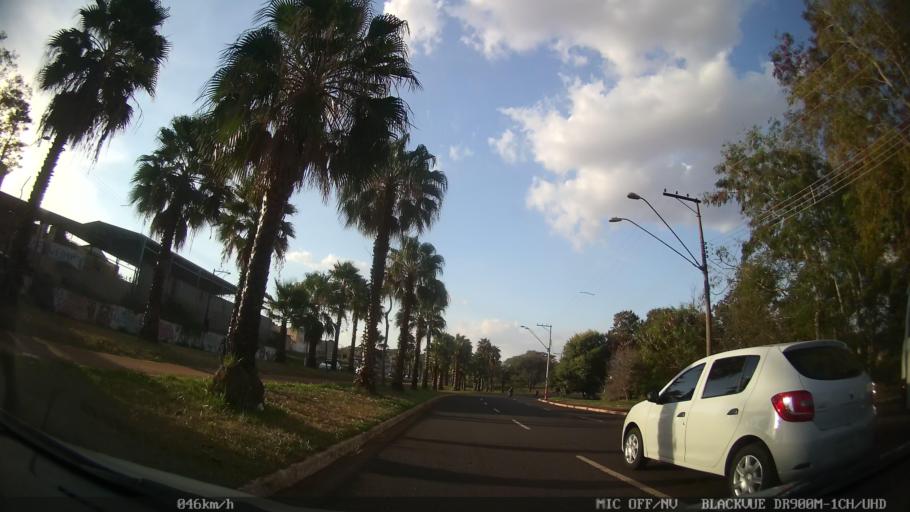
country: BR
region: Sao Paulo
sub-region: Ribeirao Preto
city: Ribeirao Preto
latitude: -21.1629
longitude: -47.8168
